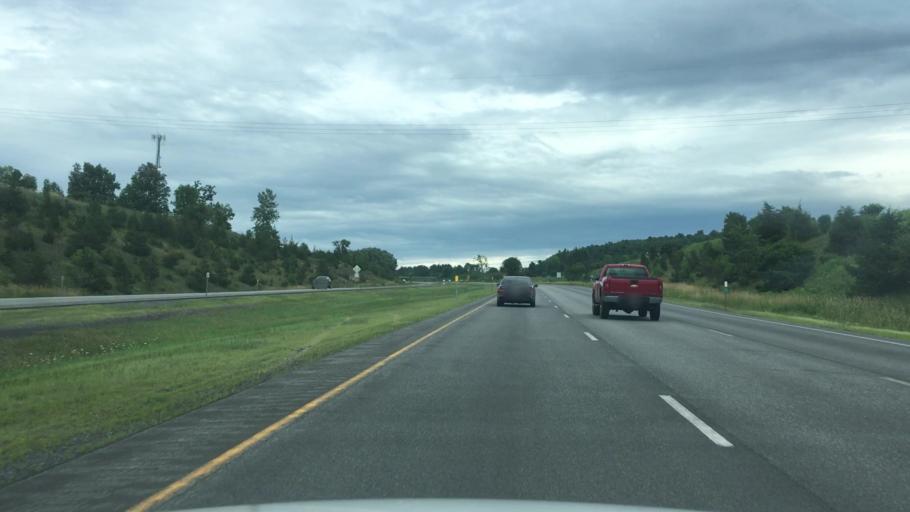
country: US
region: New York
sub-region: Schoharie County
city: Schoharie
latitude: 42.7118
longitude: -74.2881
